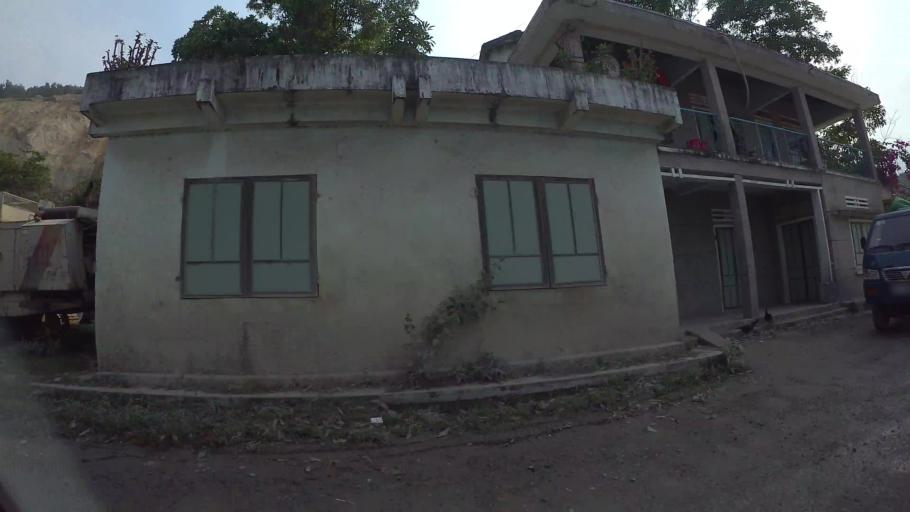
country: VN
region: Da Nang
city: Lien Chieu
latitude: 16.0379
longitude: 108.1540
